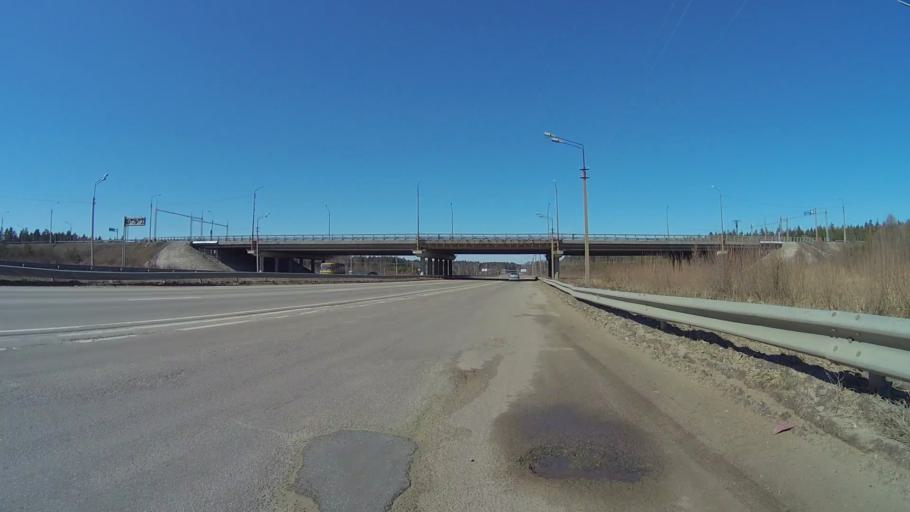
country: RU
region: Vladimir
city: Kommunar
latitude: 56.0791
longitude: 40.4748
